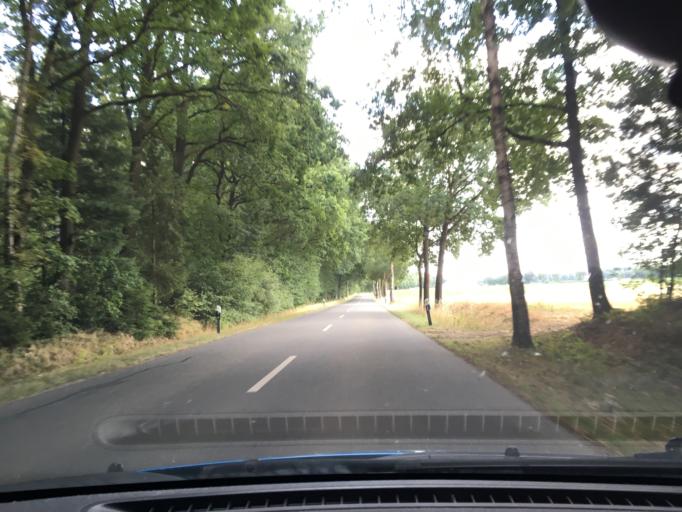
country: DE
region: Lower Saxony
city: Wriedel
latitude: 53.0462
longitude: 10.2606
